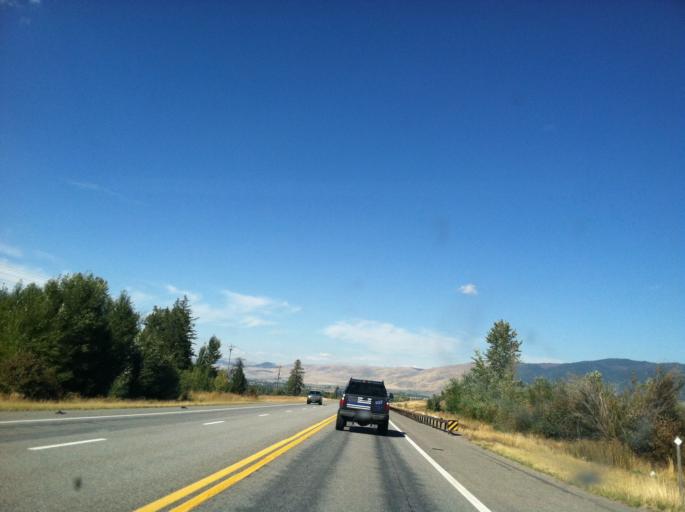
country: US
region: Montana
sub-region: Missoula County
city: Frenchtown
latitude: 47.0998
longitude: -114.0428
